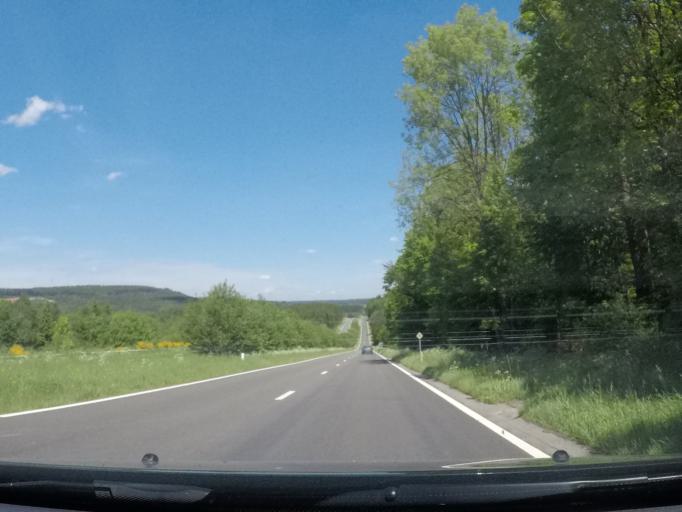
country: BE
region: Wallonia
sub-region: Province du Luxembourg
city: Saint-Hubert
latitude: 49.9551
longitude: 5.3573
